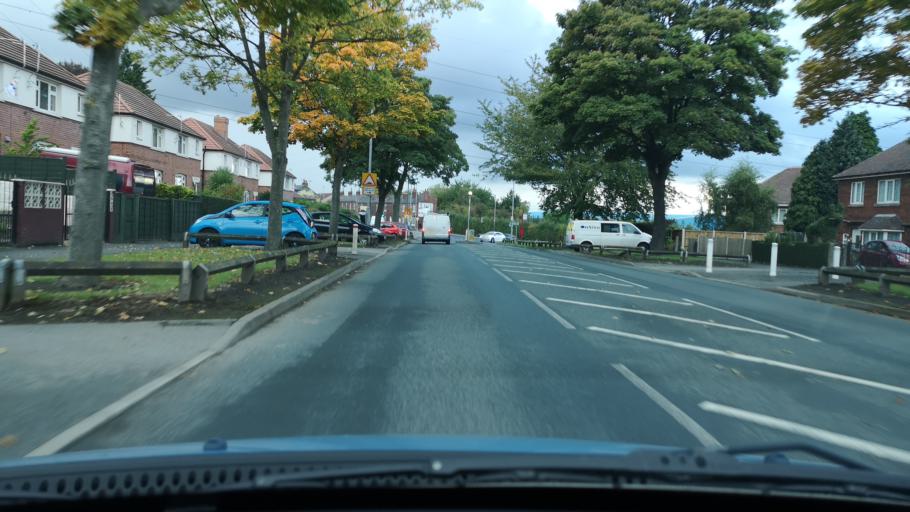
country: GB
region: England
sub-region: City and Borough of Wakefield
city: Horbury
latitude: 53.6788
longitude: -1.5438
